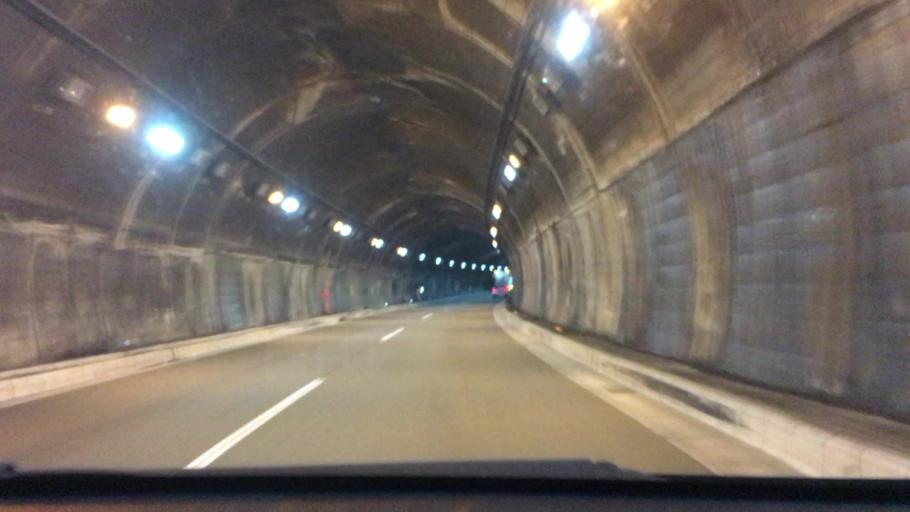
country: JP
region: Yamaguchi
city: Shimonoseki
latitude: 33.9537
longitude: 130.9801
